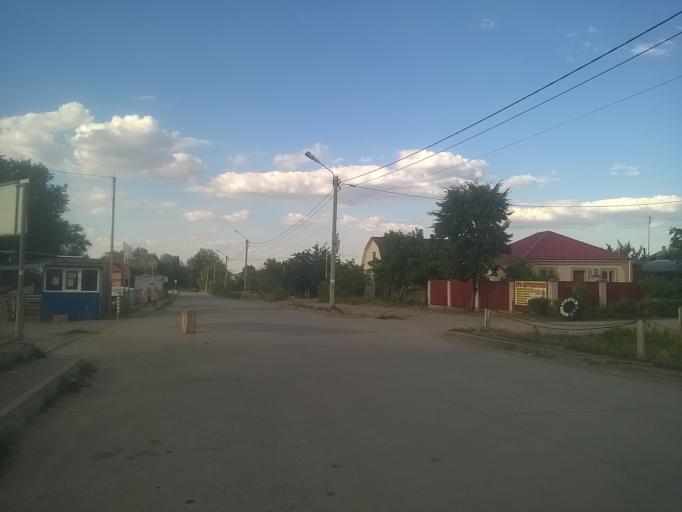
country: RU
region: Rostov
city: Donetsk
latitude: 48.3352
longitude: 39.9521
